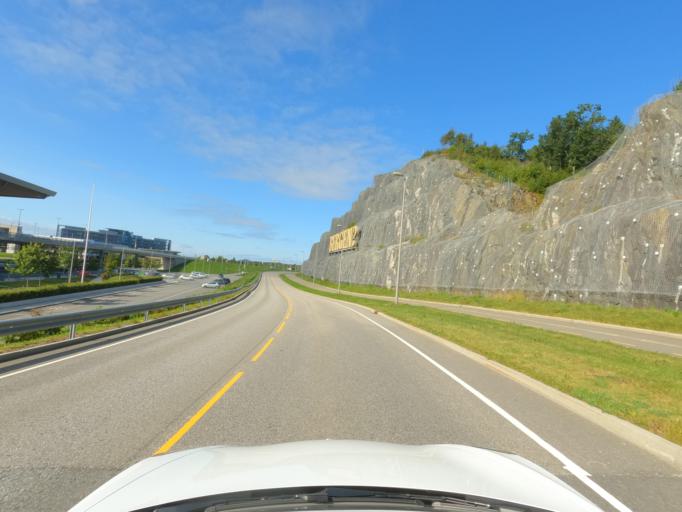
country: NO
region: Hordaland
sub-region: Bergen
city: Ytrebygda
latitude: 60.2874
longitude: 5.2341
